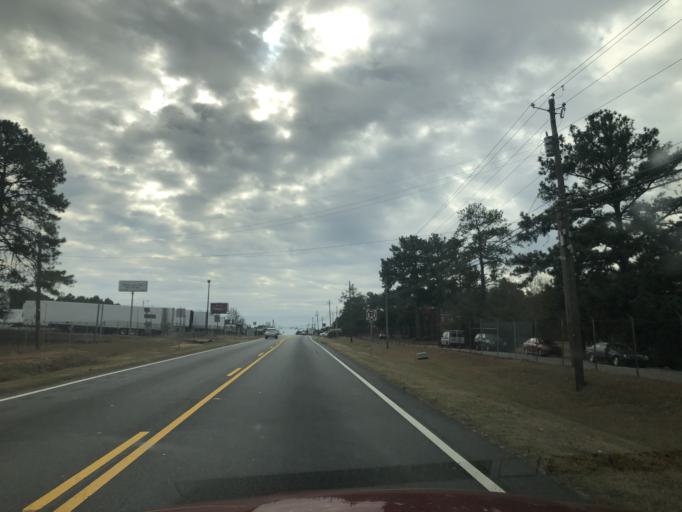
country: US
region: Georgia
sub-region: Clayton County
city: Conley
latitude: 33.6216
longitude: -84.3097
